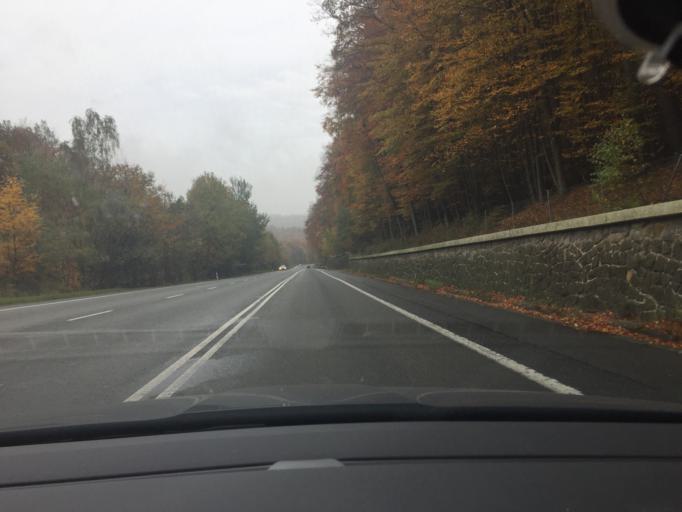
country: CZ
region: Zlin
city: Korycany
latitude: 49.1336
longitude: 17.2506
